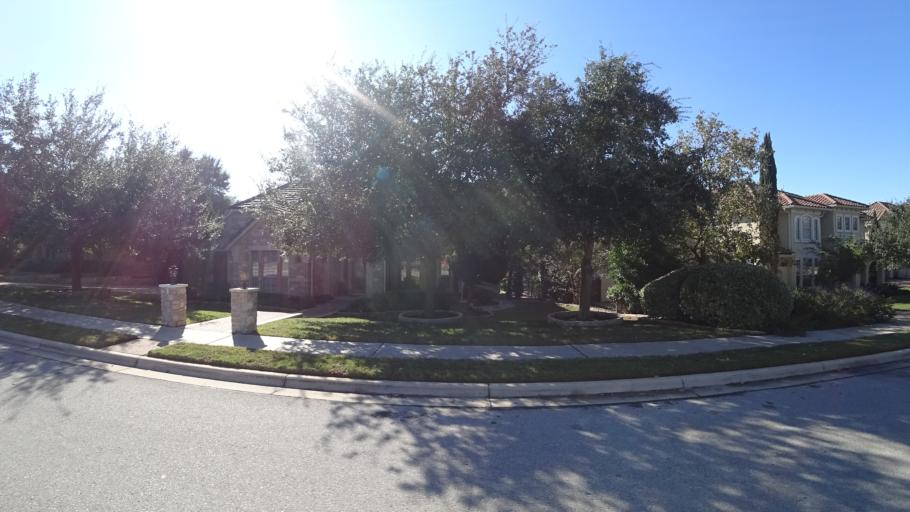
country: US
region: Texas
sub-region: Travis County
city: Bee Cave
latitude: 30.3554
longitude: -97.8895
